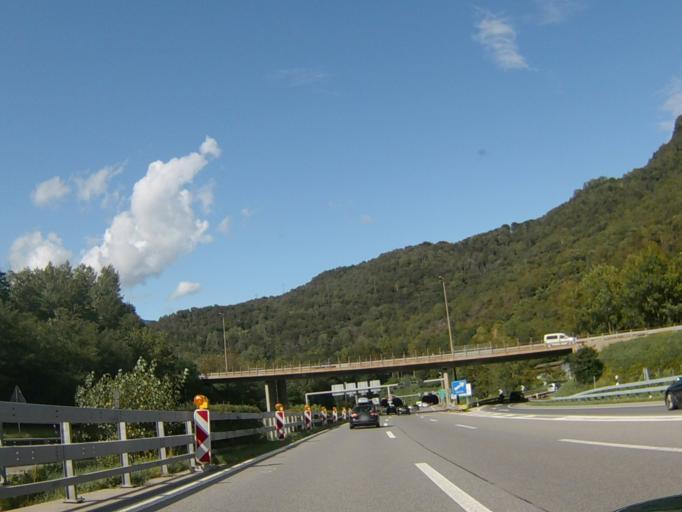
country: CH
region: Ticino
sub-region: Bellinzona District
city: Cadenazzo
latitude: 46.1294
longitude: 8.9183
